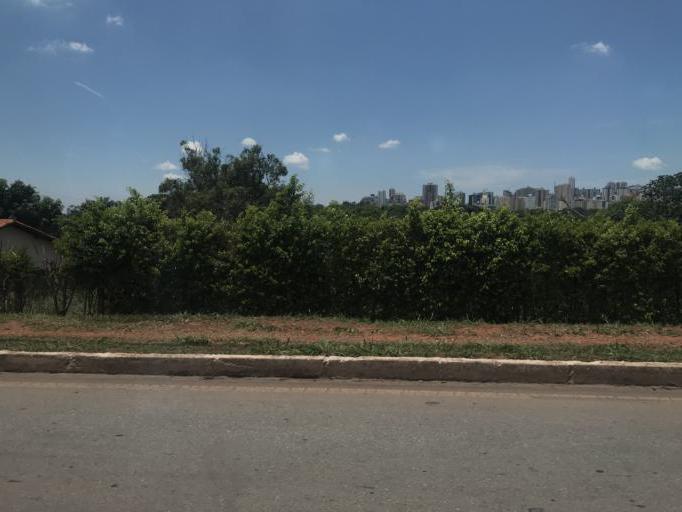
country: BR
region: Federal District
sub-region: Brasilia
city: Brasilia
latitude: -15.8193
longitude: -48.0166
